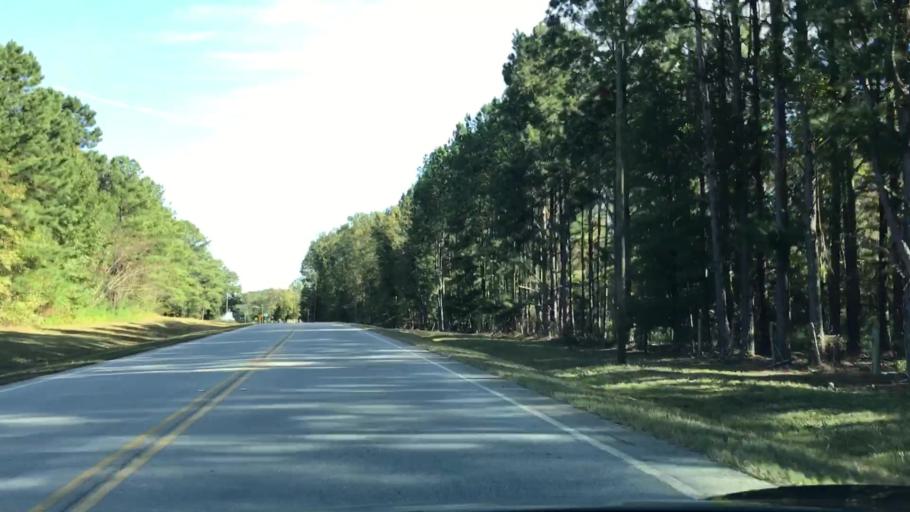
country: US
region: Georgia
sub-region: Warren County
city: Firing Range
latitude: 33.4645
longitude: -82.7109
